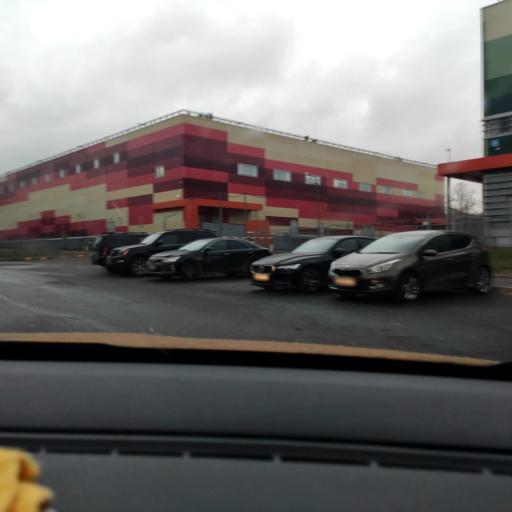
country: RU
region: Moscow
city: Mikhalkovo
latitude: 55.6820
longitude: 37.4253
